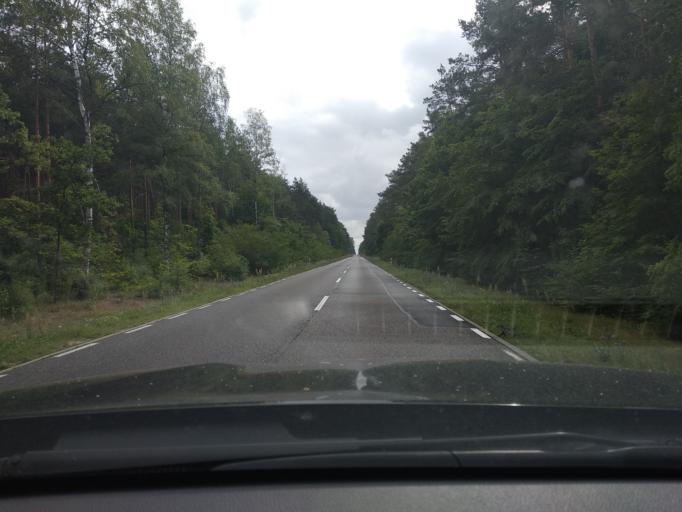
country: PL
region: Masovian Voivodeship
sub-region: Powiat pultuski
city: Obryte
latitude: 52.6448
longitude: 21.2599
